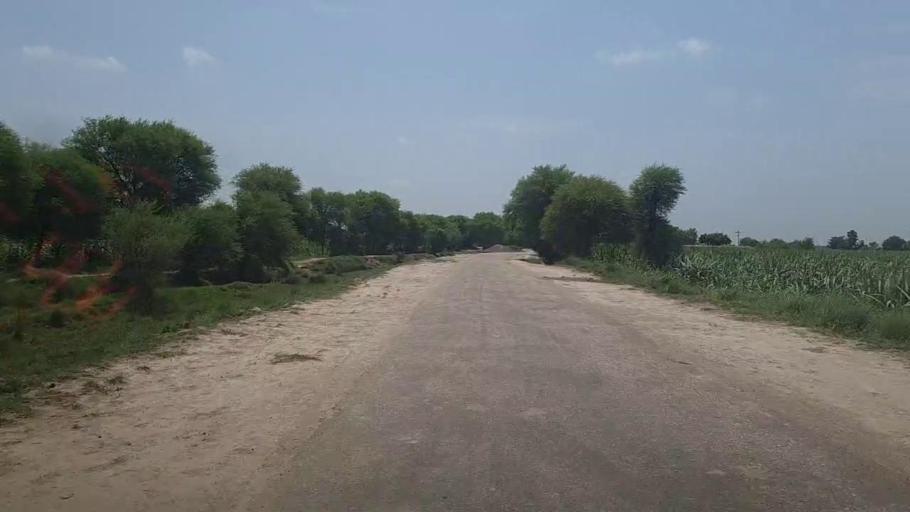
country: PK
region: Sindh
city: Ubauro
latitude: 28.2841
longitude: 69.8089
